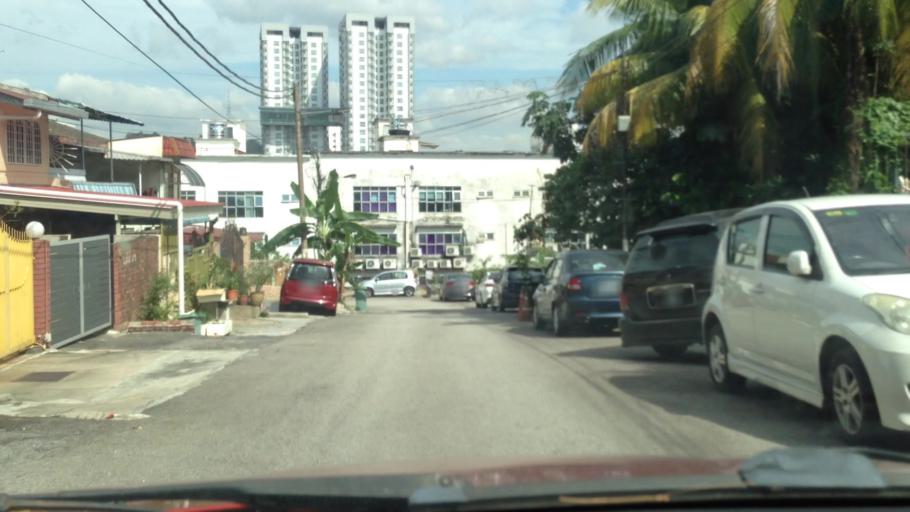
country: MY
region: Kuala Lumpur
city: Kuala Lumpur
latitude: 3.0915
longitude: 101.6780
